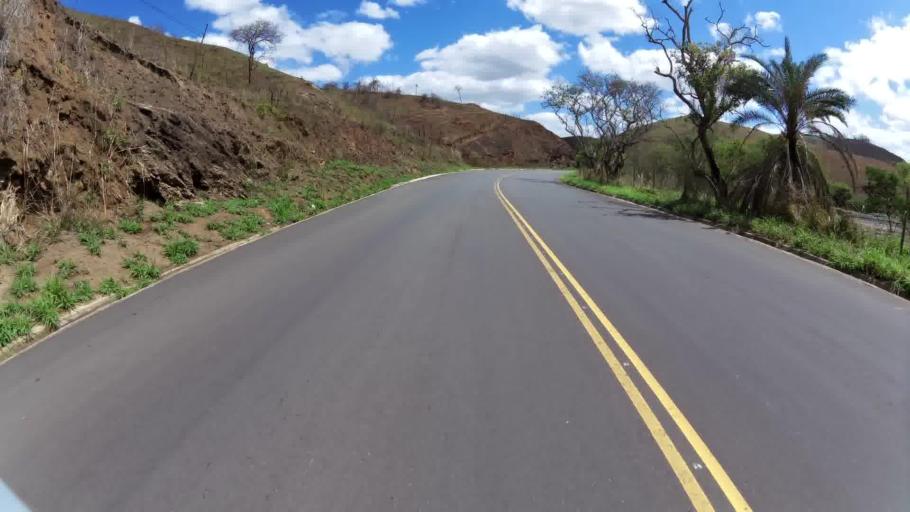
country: BR
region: Rio de Janeiro
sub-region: Itaperuna
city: Itaperuna
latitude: -21.2713
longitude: -41.7790
